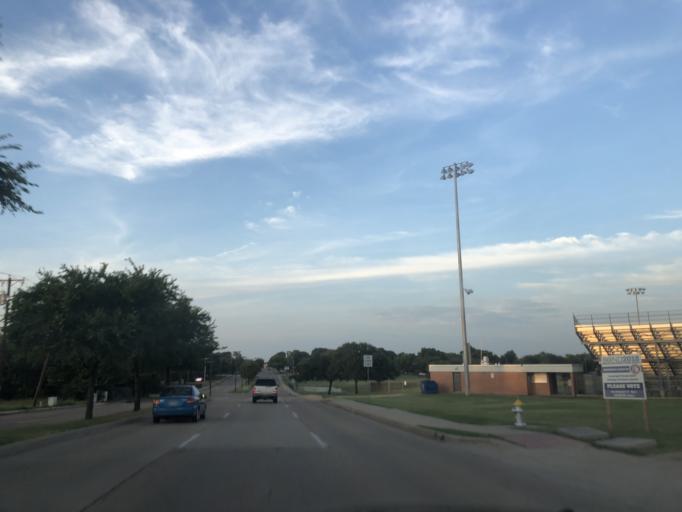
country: US
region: Texas
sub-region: Dallas County
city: Mesquite
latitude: 32.8056
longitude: -96.6413
